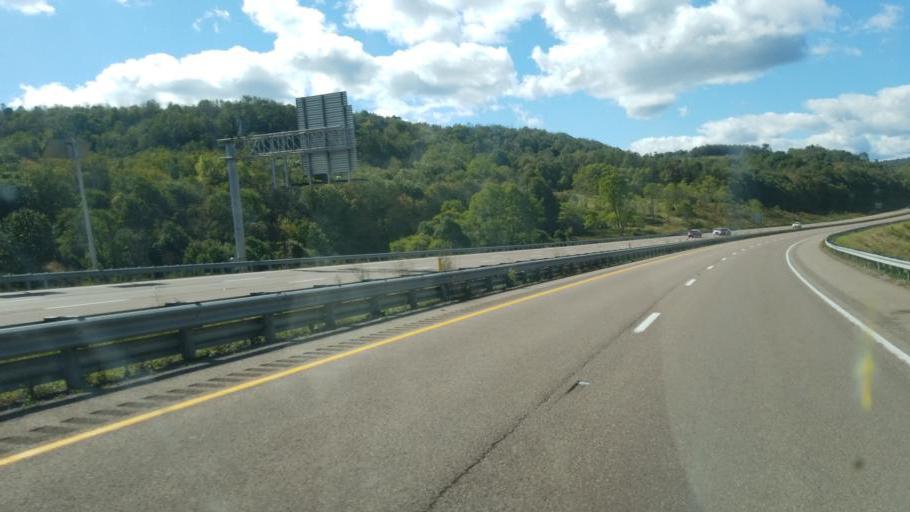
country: US
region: Pennsylvania
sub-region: Somerset County
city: Meyersdale
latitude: 39.6957
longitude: -79.2751
